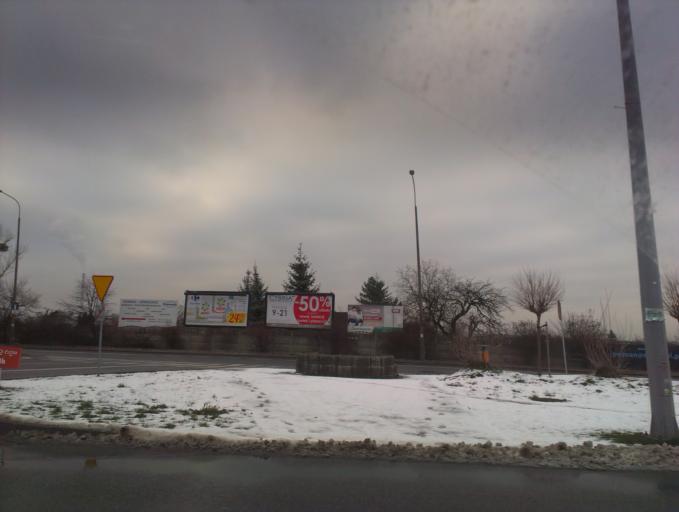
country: PL
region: Greater Poland Voivodeship
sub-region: Poznan
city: Poznan
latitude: 52.4328
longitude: 16.9536
